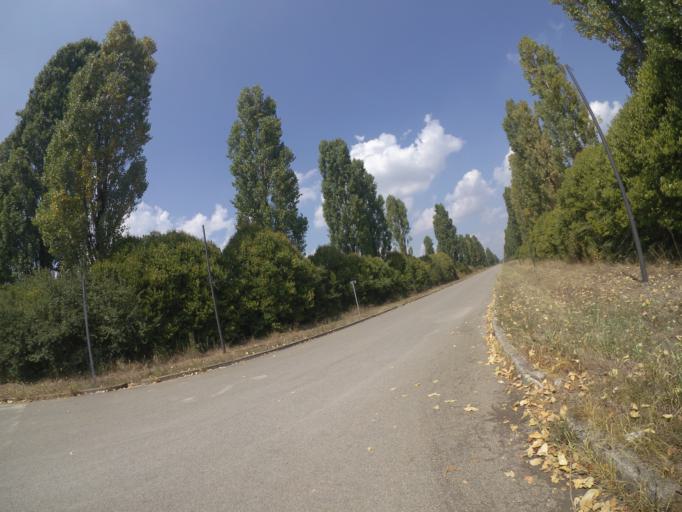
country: IT
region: Friuli Venezia Giulia
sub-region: Provincia di Udine
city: Codroipo
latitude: 45.9535
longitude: 13.0112
